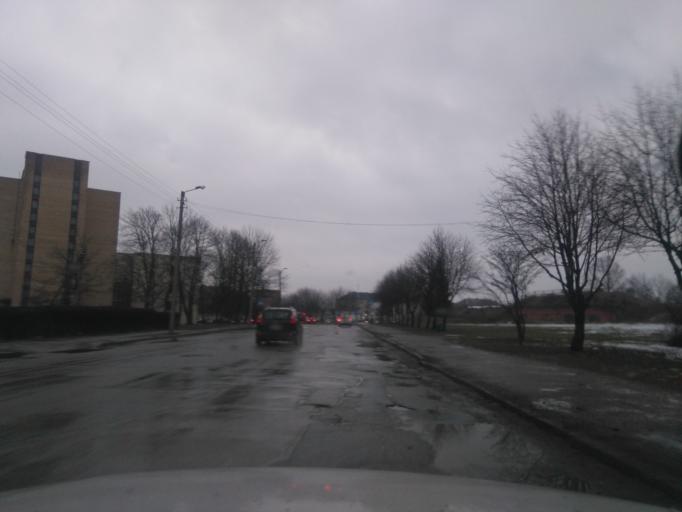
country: LT
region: Kauno apskritis
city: Dainava (Kaunas)
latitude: 54.8957
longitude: 23.9563
